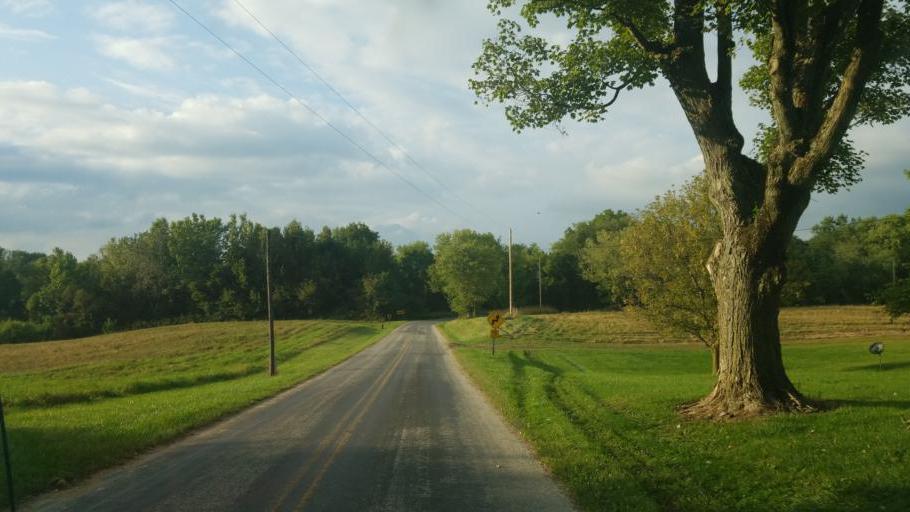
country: US
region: Ohio
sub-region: Wayne County
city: Shreve
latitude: 40.7459
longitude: -82.1316
